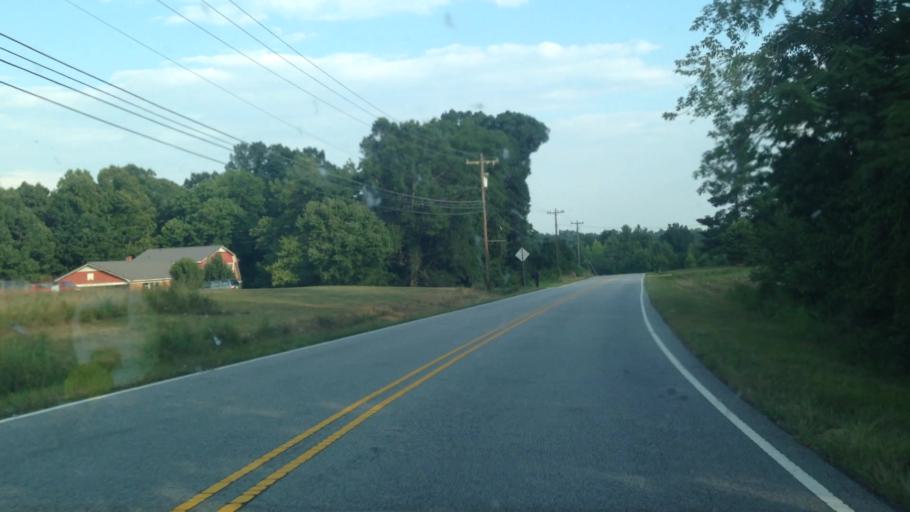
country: US
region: North Carolina
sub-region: Davidson County
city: Wallburg
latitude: 35.9690
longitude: -80.0841
